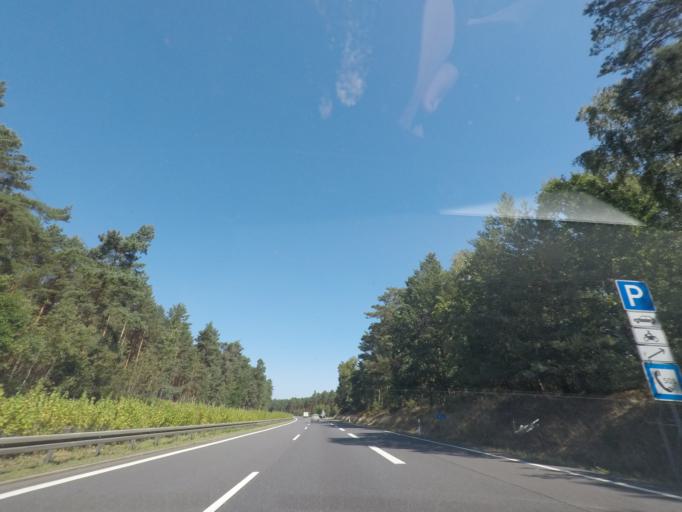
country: DE
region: Brandenburg
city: Bronkow
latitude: 51.6943
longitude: 13.9018
